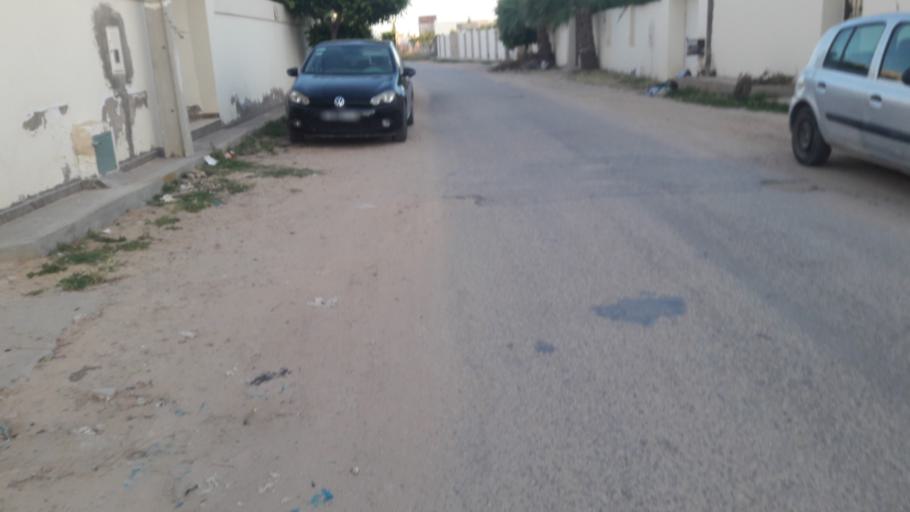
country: TN
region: Safaqis
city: Sfax
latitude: 34.8109
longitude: 10.7427
